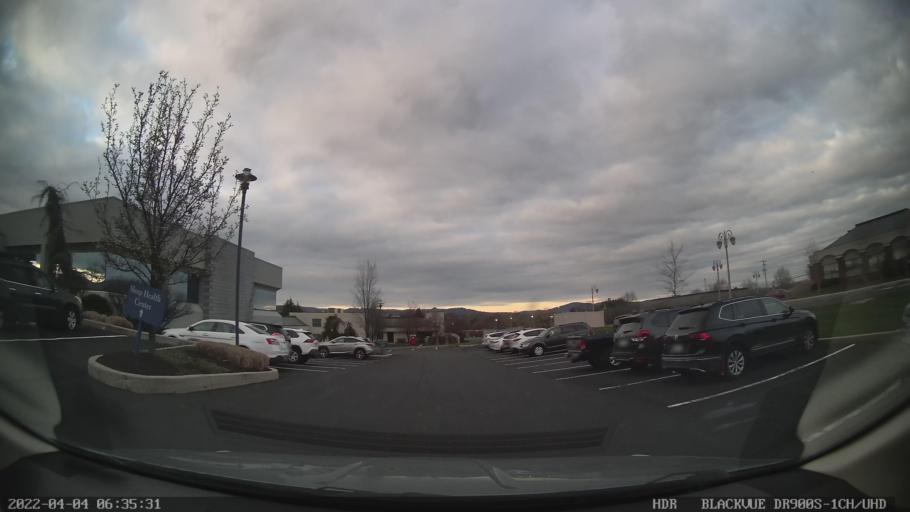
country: US
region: Pennsylvania
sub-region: Berks County
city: Spring Ridge
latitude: 40.3436
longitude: -75.9884
